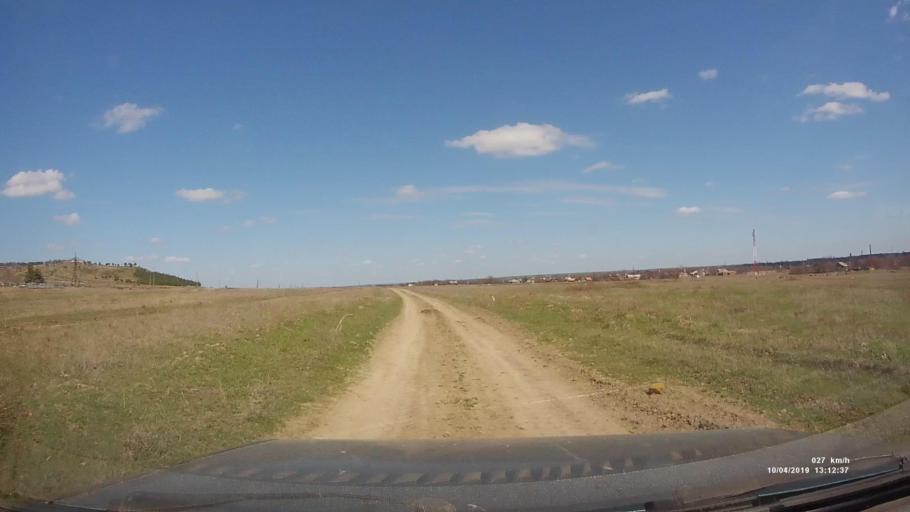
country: RU
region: Rostov
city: Masalovka
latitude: 48.4135
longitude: 40.2562
